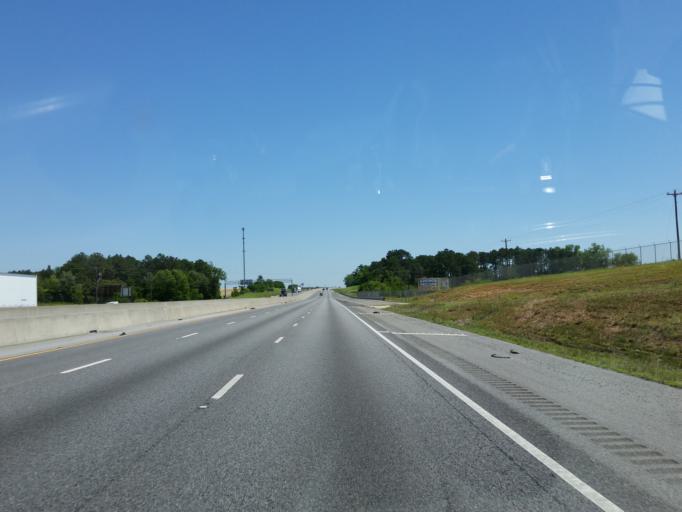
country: US
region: Georgia
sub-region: Turner County
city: Ashburn
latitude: 31.6259
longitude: -83.5760
